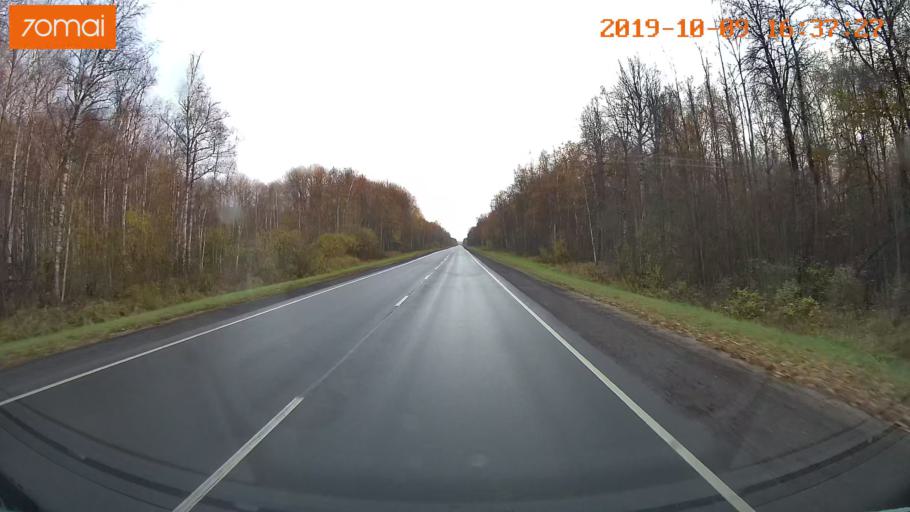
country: RU
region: Kostroma
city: Volgorechensk
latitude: 57.5268
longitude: 41.0248
